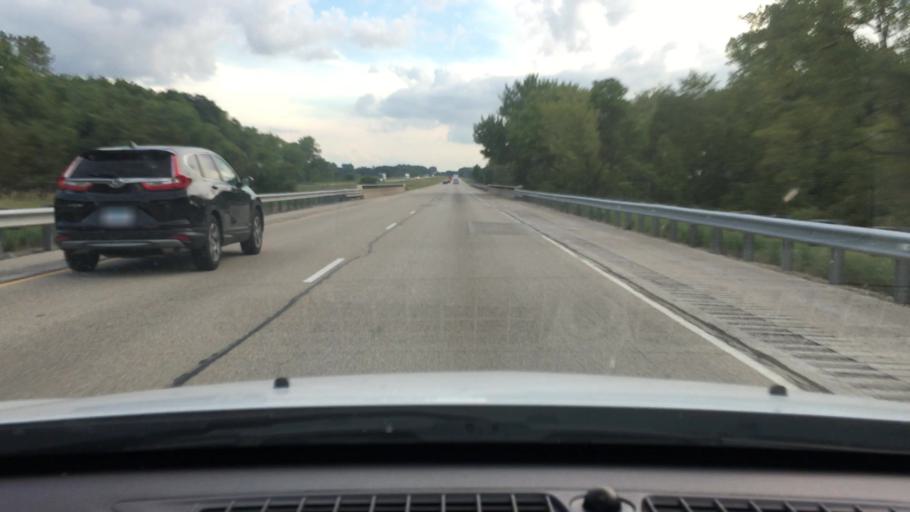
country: US
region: Illinois
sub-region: McLean County
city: Twin Grove
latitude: 40.3742
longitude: -89.0972
